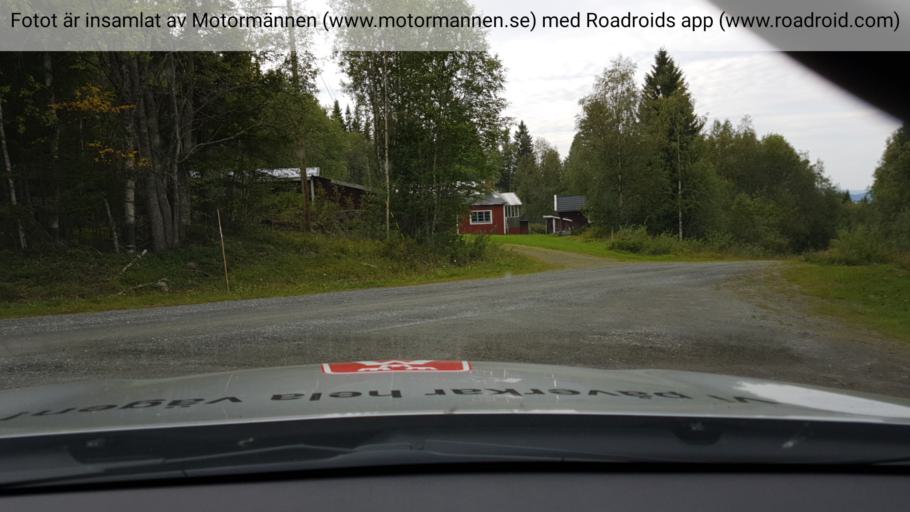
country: SE
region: Jaemtland
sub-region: Krokoms Kommun
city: Valla
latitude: 63.5932
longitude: 13.9986
